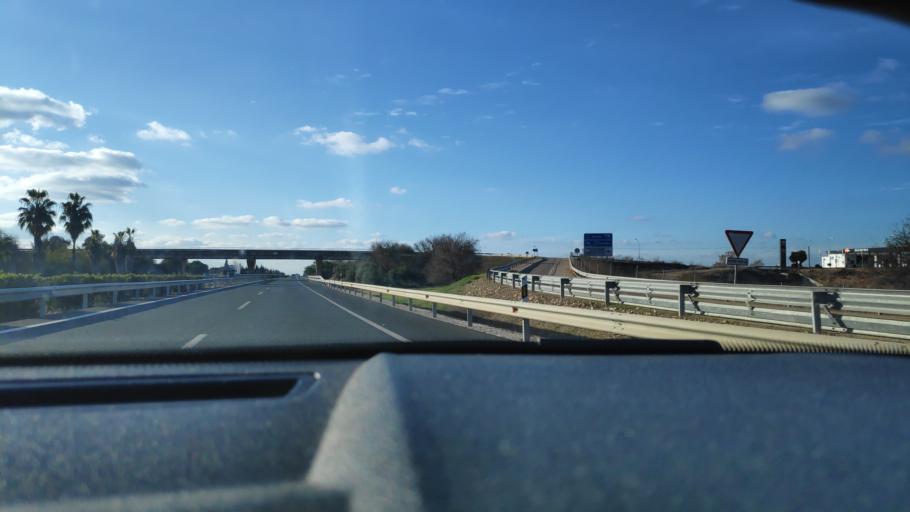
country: ES
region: Andalusia
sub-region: Provincia de Sevilla
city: La Luisiana
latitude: 37.5229
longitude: -5.1929
